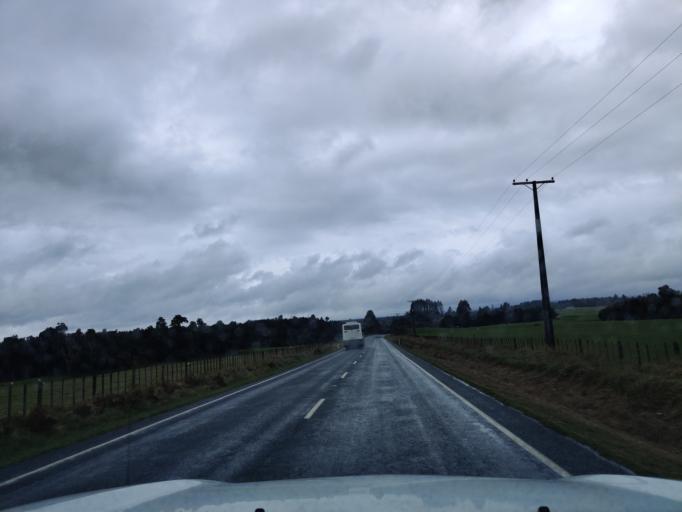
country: NZ
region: Manawatu-Wanganui
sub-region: Ruapehu District
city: Waiouru
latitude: -39.3525
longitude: 175.3589
